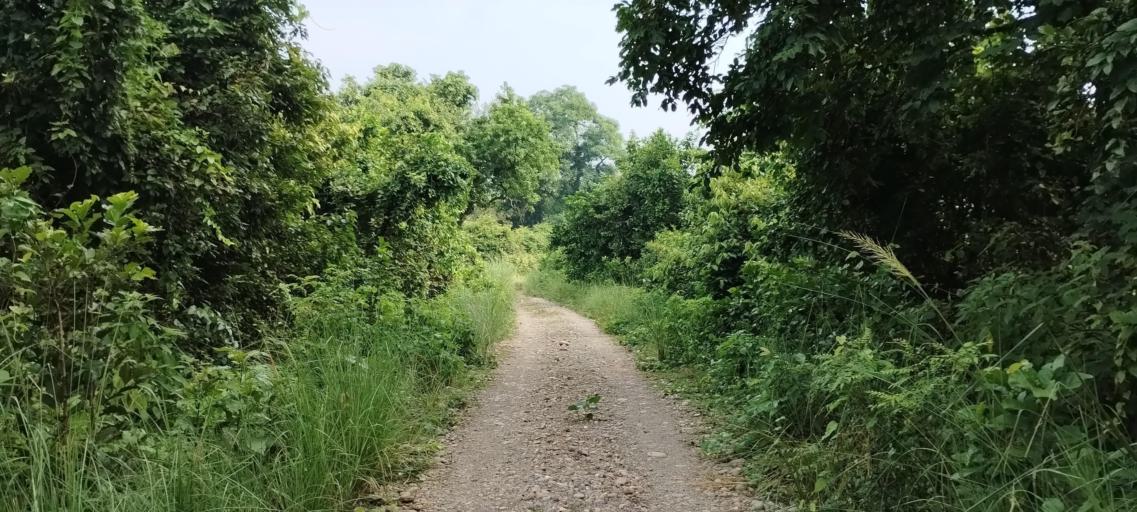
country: NP
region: Far Western
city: Tikapur
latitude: 28.4573
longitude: 81.2423
